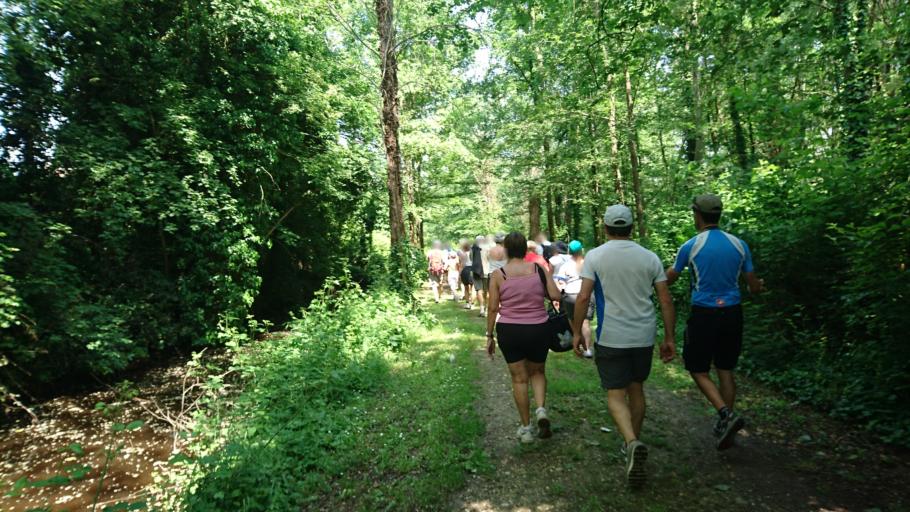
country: IT
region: Veneto
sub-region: Provincia di Venezia
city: Campagna Lupia
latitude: 45.3632
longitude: 12.1380
